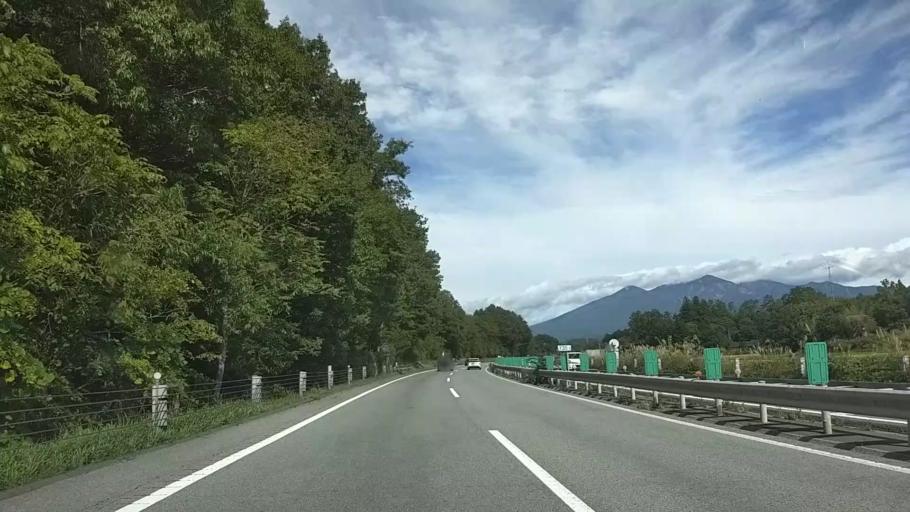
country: JP
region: Yamanashi
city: Nirasaki
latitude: 35.7950
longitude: 138.3971
